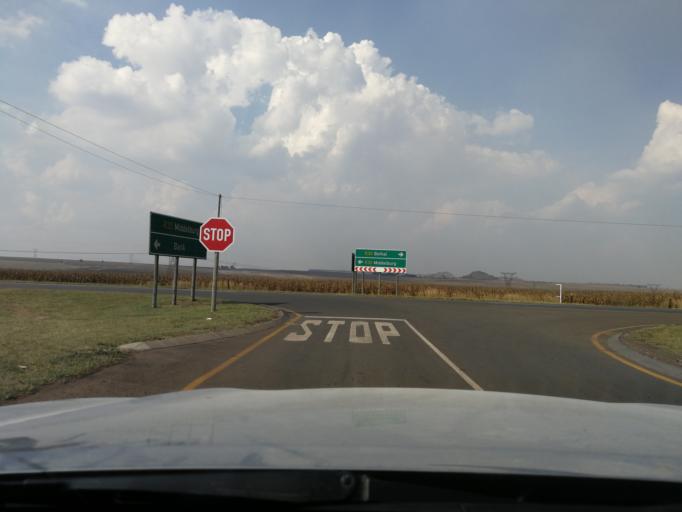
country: ZA
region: Mpumalanga
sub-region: Nkangala District Municipality
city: Middelburg
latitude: -25.9808
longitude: 29.4797
